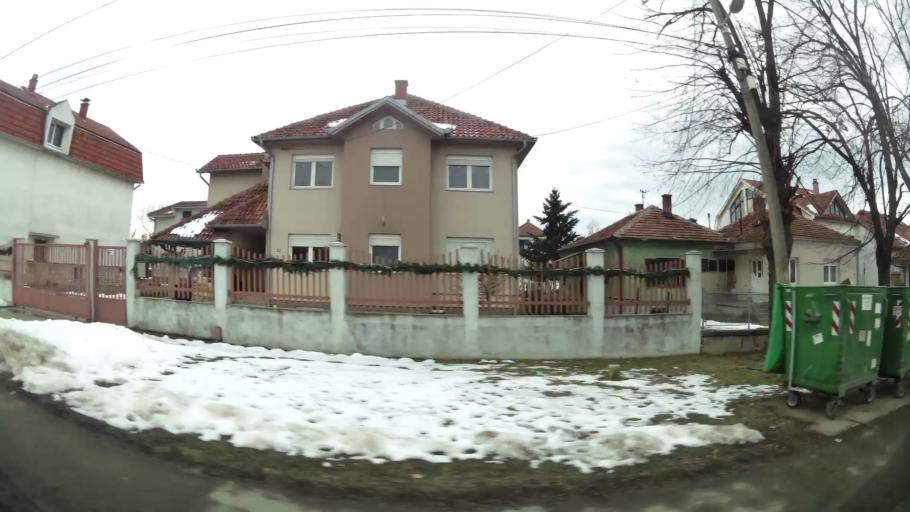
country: RS
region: Central Serbia
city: Sremcica
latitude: 44.7287
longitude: 20.3823
